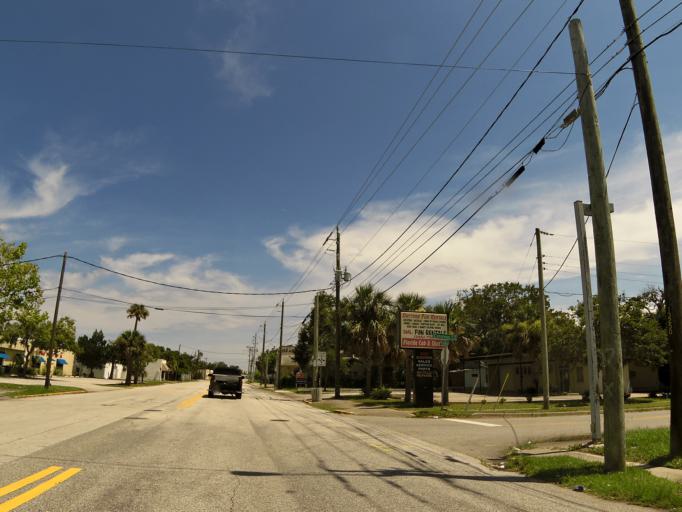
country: US
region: Florida
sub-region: Volusia County
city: Daytona Beach
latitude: 29.2282
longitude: -81.0266
